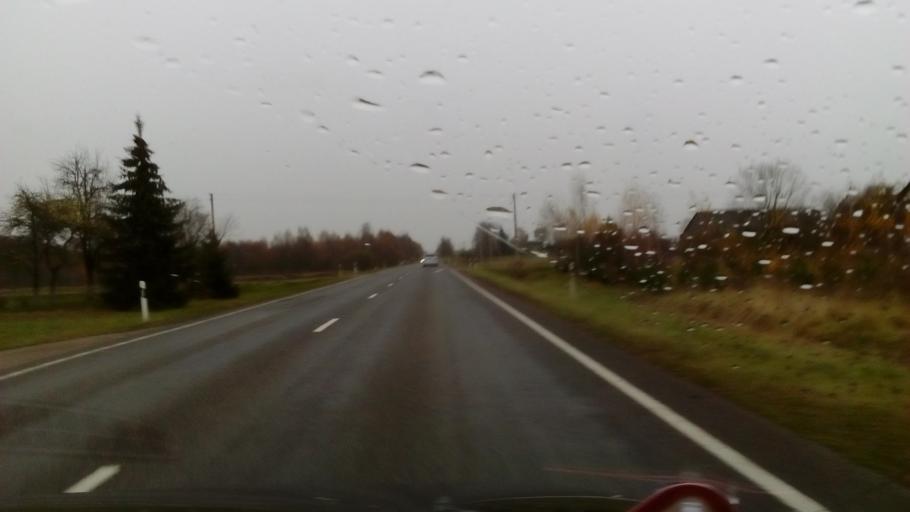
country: LT
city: Simnas
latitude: 54.5608
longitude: 23.6933
